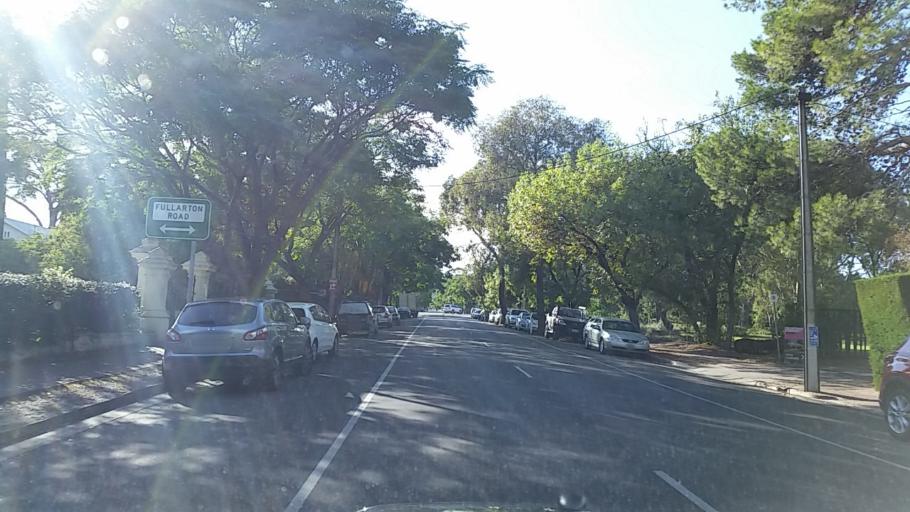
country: AU
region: South Australia
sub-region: Unley
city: Fullarton
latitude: -34.9569
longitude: 138.6240
